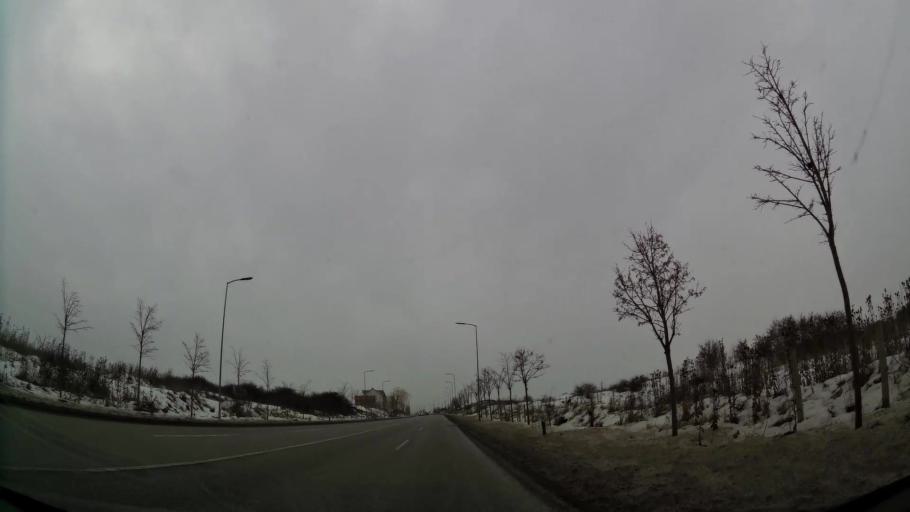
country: XK
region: Pristina
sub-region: Komuna e Prishtines
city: Pristina
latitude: 42.7048
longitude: 21.1557
